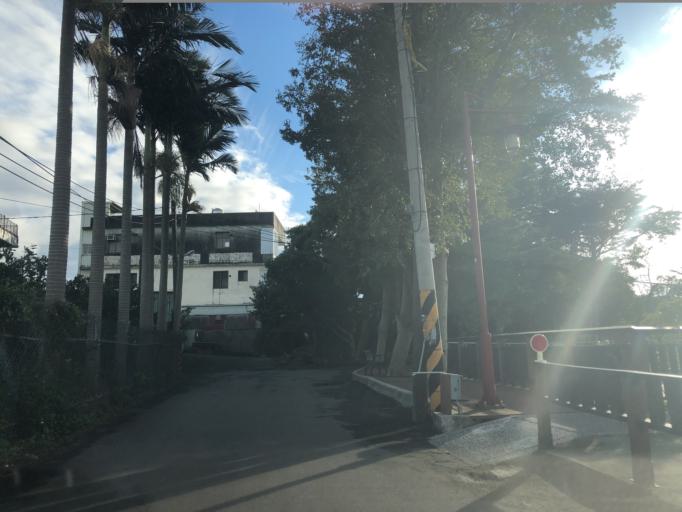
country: TW
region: Taiwan
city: Daxi
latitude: 24.9049
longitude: 121.2665
